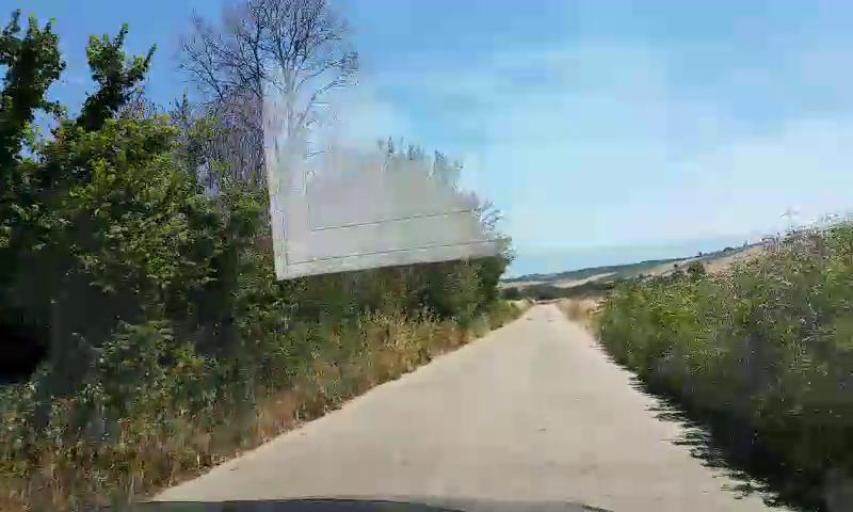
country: IT
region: Molise
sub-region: Provincia di Campobasso
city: Guglionesi
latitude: 41.9391
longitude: 14.8928
